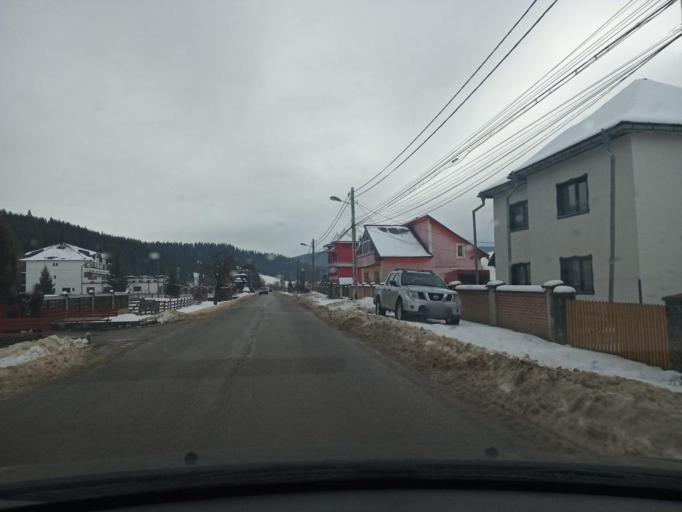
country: RO
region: Suceava
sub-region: Comuna Manastirea Humorului
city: Manastirea Humorului
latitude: 47.5773
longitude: 25.8750
